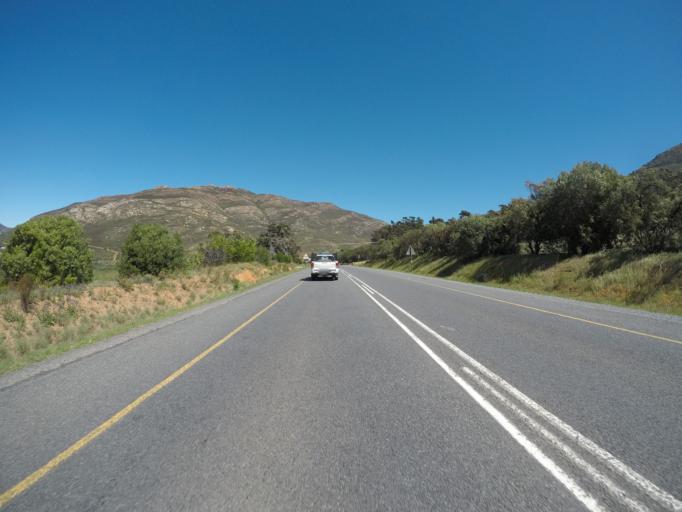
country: ZA
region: Western Cape
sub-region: Cape Winelands District Municipality
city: Ceres
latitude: -33.3141
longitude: 19.0941
